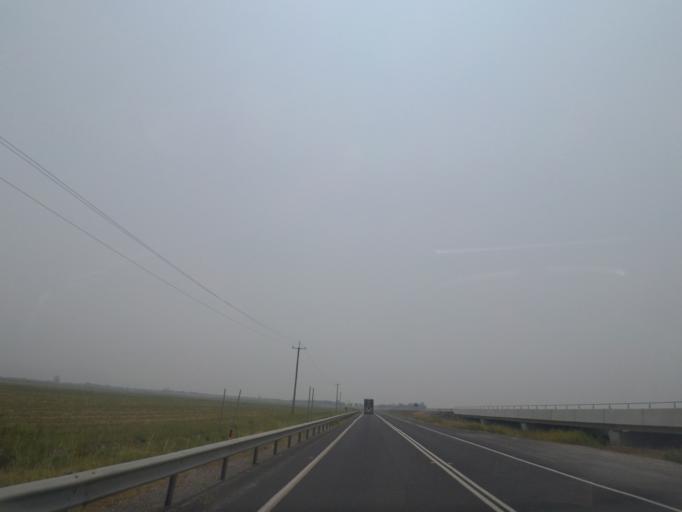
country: AU
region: New South Wales
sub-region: Clarence Valley
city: Maclean
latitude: -29.4129
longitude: 153.2413
